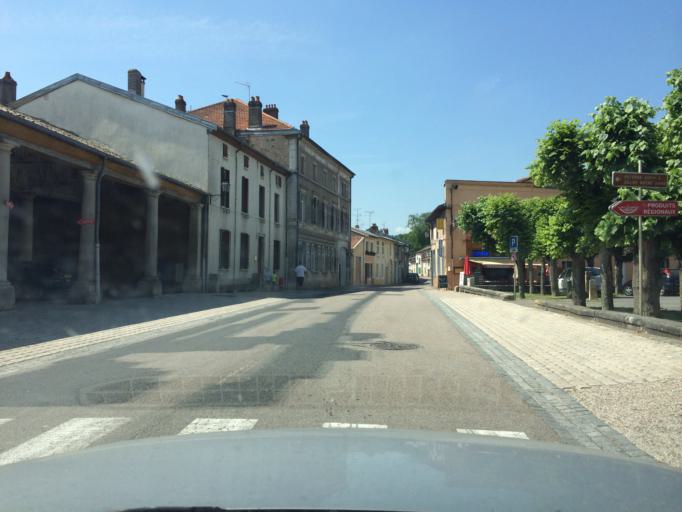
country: FR
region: Lorraine
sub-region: Departement de la Meuse
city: Vacon
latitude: 48.6869
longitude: 5.6181
